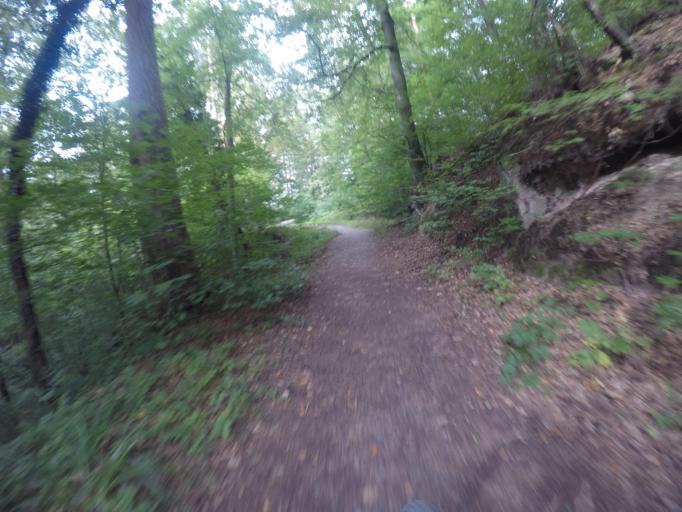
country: DE
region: Baden-Wuerttemberg
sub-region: Regierungsbezirk Stuttgart
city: Stuttgart
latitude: 48.7481
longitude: 9.1449
